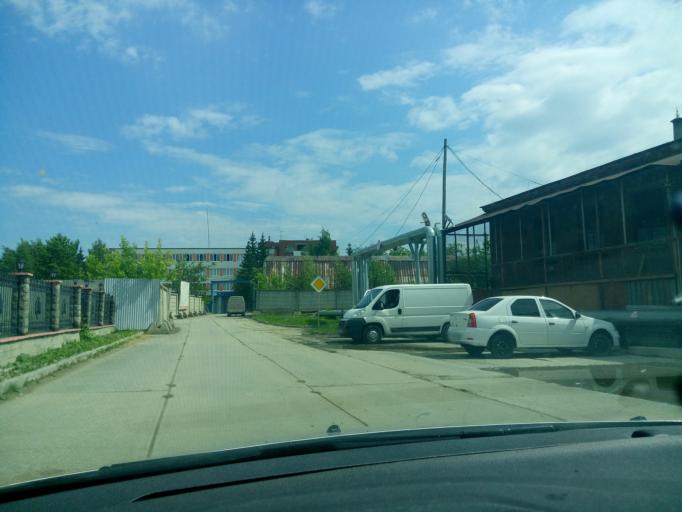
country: RU
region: Sverdlovsk
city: Yekaterinburg
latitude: 56.8576
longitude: 60.6622
